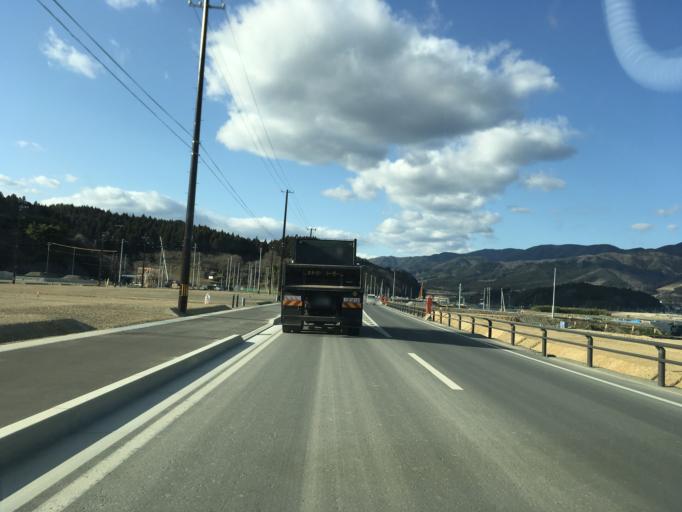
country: JP
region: Iwate
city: Ofunato
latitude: 39.0081
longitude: 141.6165
